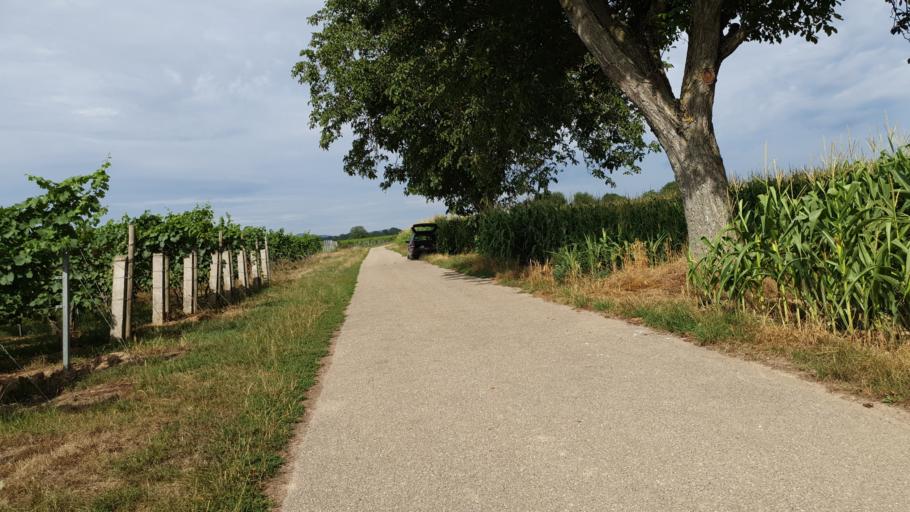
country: DE
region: Rheinland-Pfalz
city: Hergersweiler
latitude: 49.1137
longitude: 8.0954
